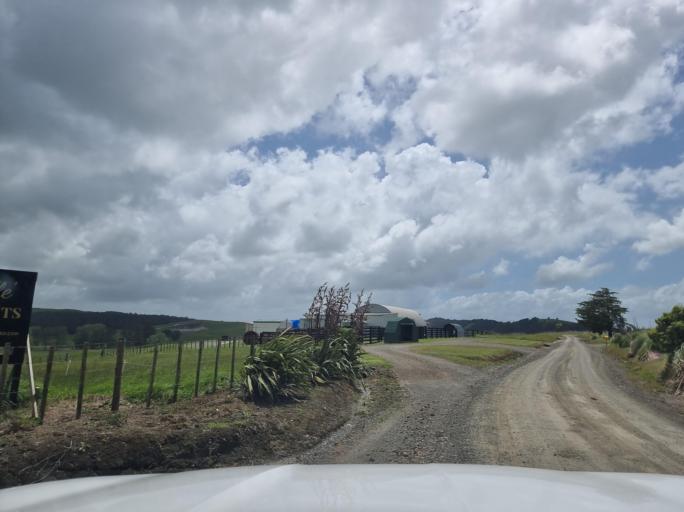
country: NZ
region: Northland
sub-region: Kaipara District
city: Dargaville
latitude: -36.0986
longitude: 174.1292
